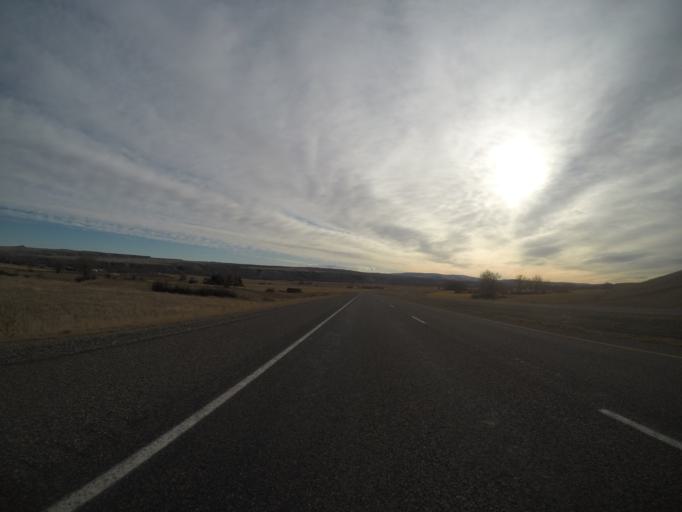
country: US
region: Montana
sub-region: Yellowstone County
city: Laurel
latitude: 45.5425
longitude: -108.8569
